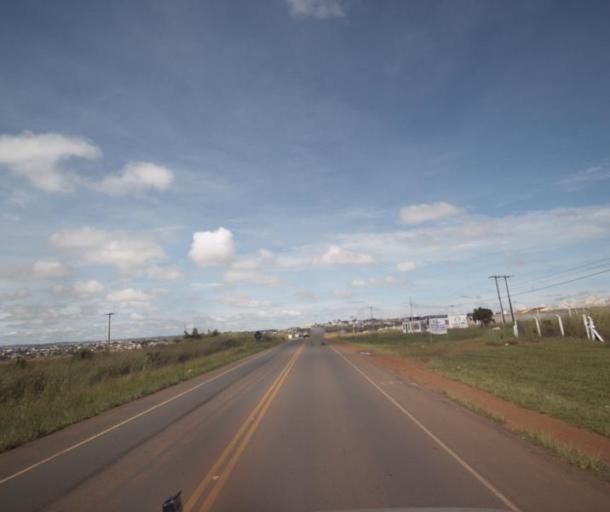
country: BR
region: Goias
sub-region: Anapolis
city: Anapolis
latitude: -16.2609
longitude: -48.9376
